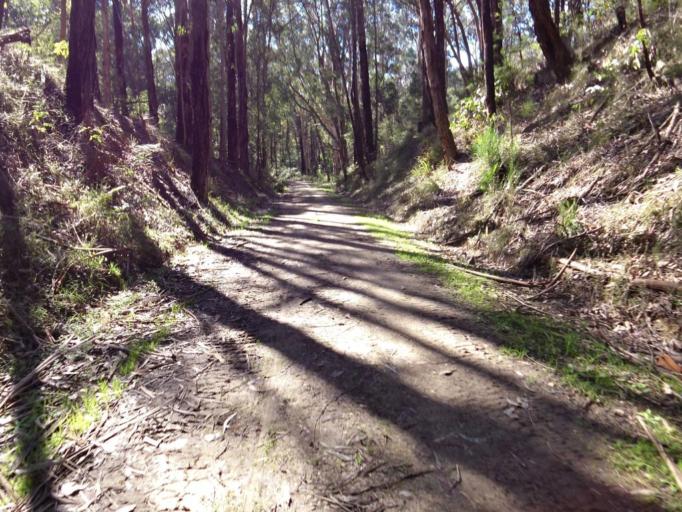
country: AU
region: Victoria
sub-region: Baw Baw
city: Warragul
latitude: -38.0623
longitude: 145.9459
